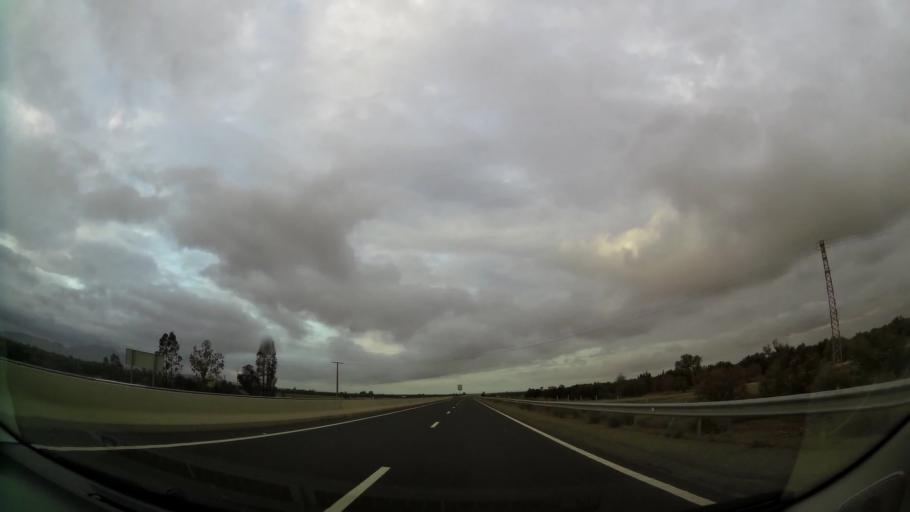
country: MA
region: Taza-Al Hoceima-Taounate
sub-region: Taza
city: Guercif
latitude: 34.3554
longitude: -3.3048
